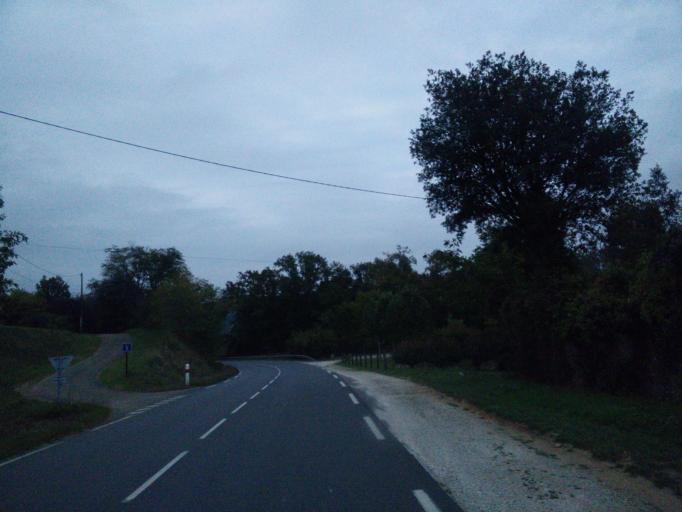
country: FR
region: Aquitaine
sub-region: Departement de la Dordogne
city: Carsac-Aillac
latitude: 44.8286
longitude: 1.2794
